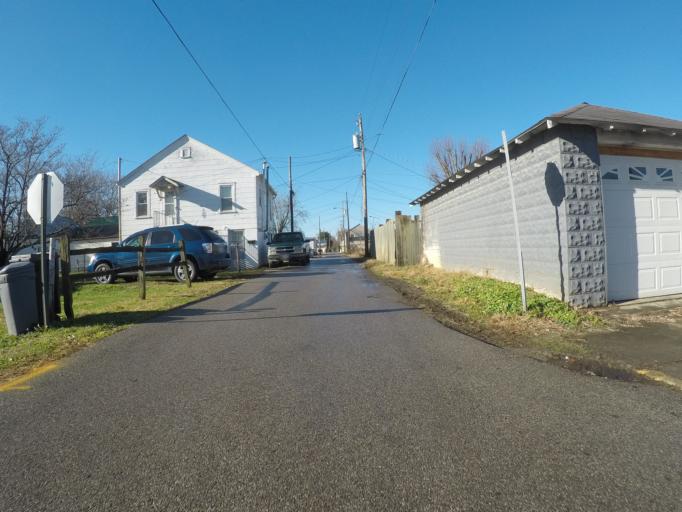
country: US
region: West Virginia
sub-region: Cabell County
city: Huntington
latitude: 38.4272
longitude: -82.4537
